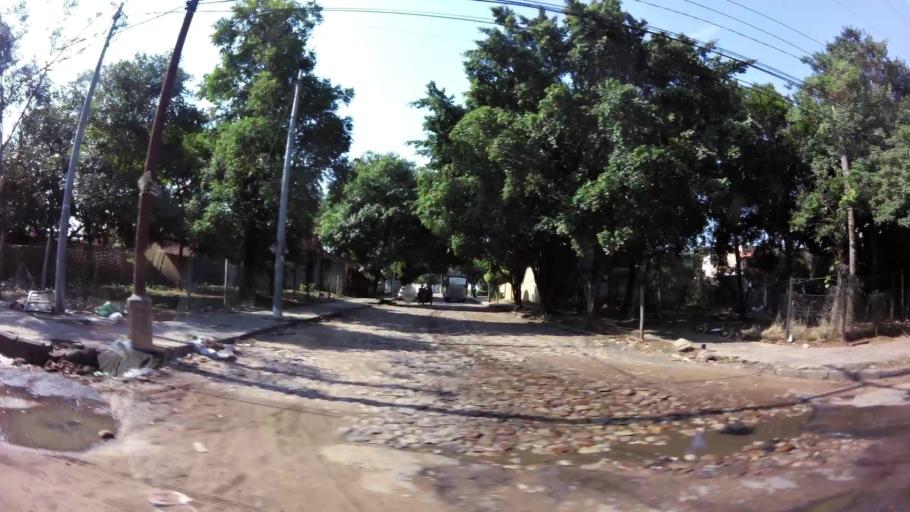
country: PY
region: Asuncion
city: Asuncion
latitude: -25.3229
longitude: -57.6367
